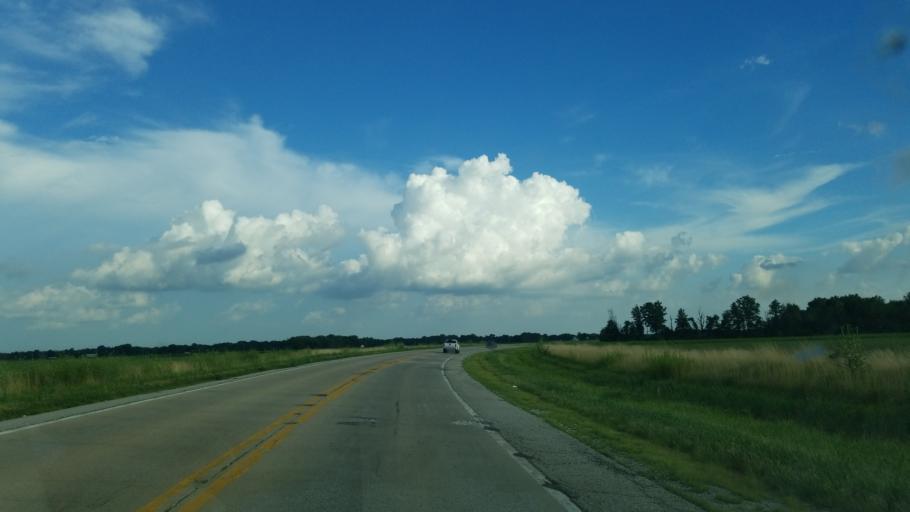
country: US
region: Illinois
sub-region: Marion County
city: Sandoval
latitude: 38.6014
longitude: -89.1088
